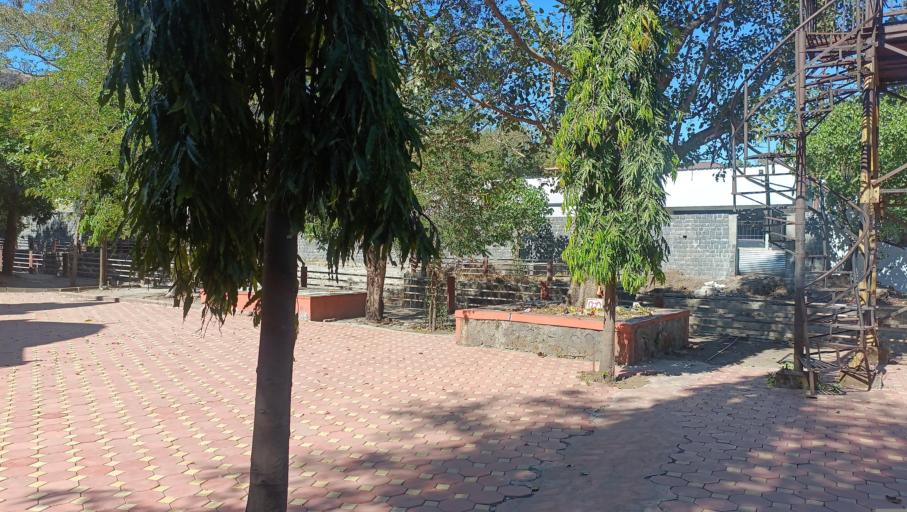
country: IN
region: Maharashtra
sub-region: Nashik Division
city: Trimbak
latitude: 19.9321
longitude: 73.5321
